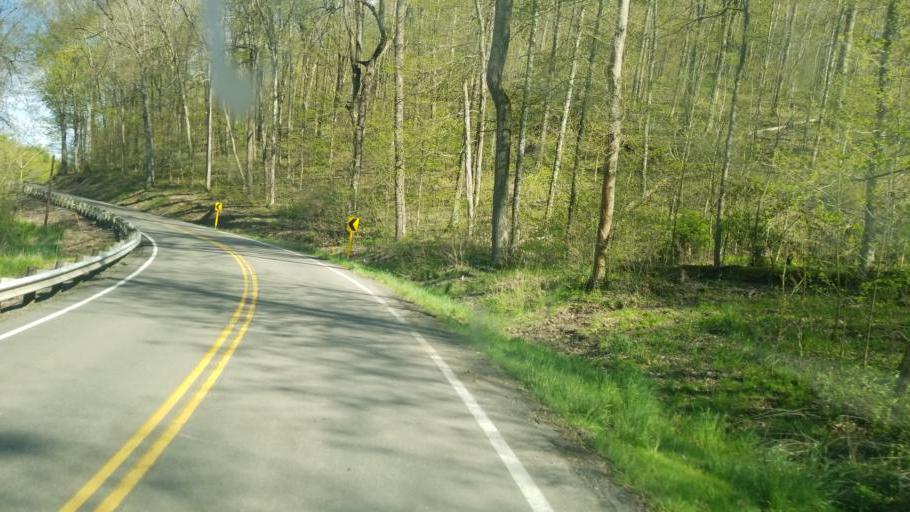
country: US
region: Ohio
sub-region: Coshocton County
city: Coshocton
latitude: 40.3605
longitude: -81.9797
